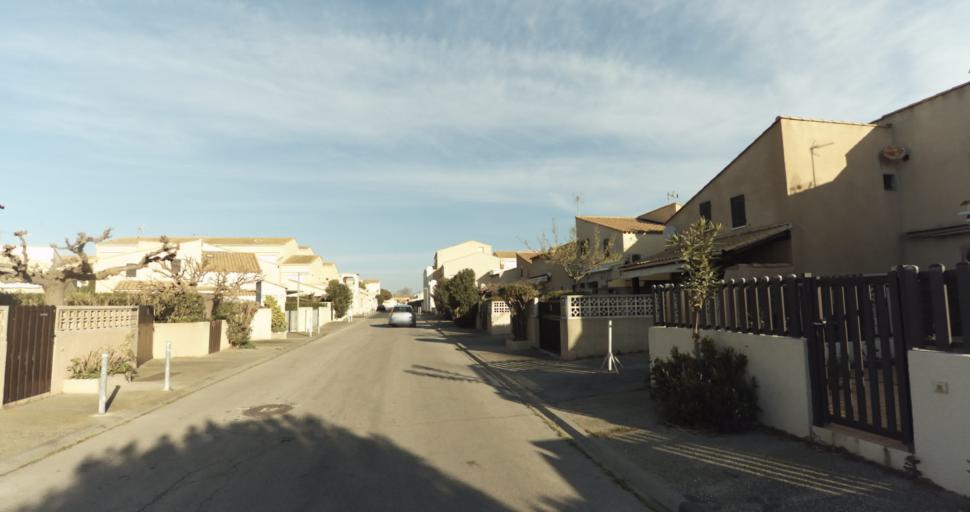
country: FR
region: Languedoc-Roussillon
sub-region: Departement de l'Herault
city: Marseillan
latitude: 43.3145
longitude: 3.5482
